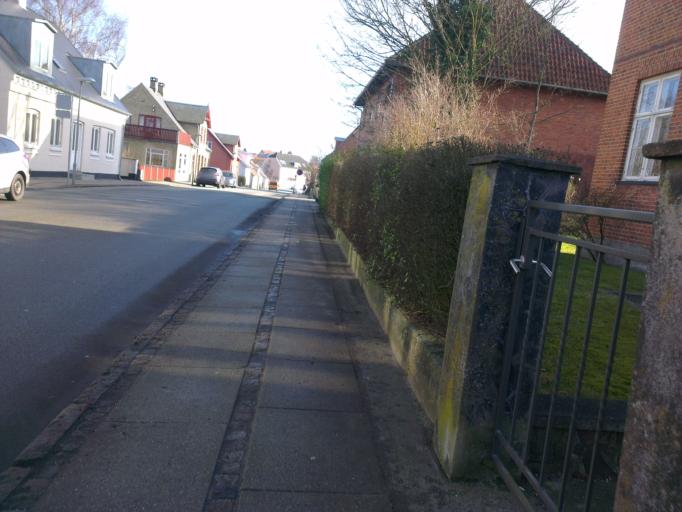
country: DK
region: Capital Region
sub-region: Frederikssund Kommune
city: Frederikssund
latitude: 55.8409
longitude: 12.0593
